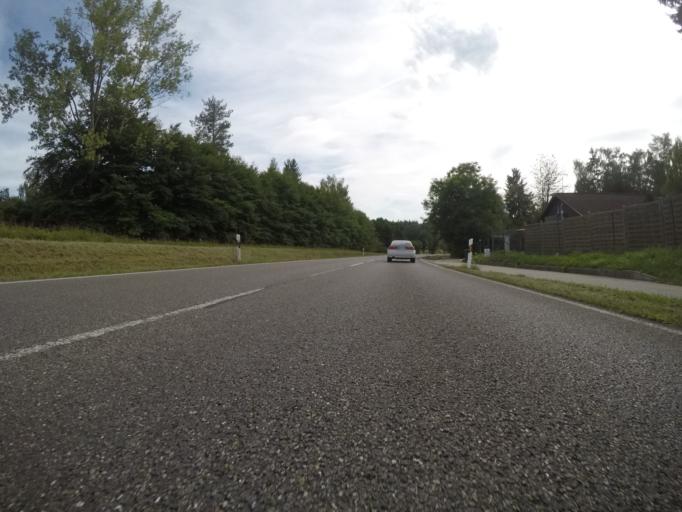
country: DE
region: Baden-Wuerttemberg
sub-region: Regierungsbezirk Stuttgart
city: Rutesheim
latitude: 48.7977
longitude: 8.9393
